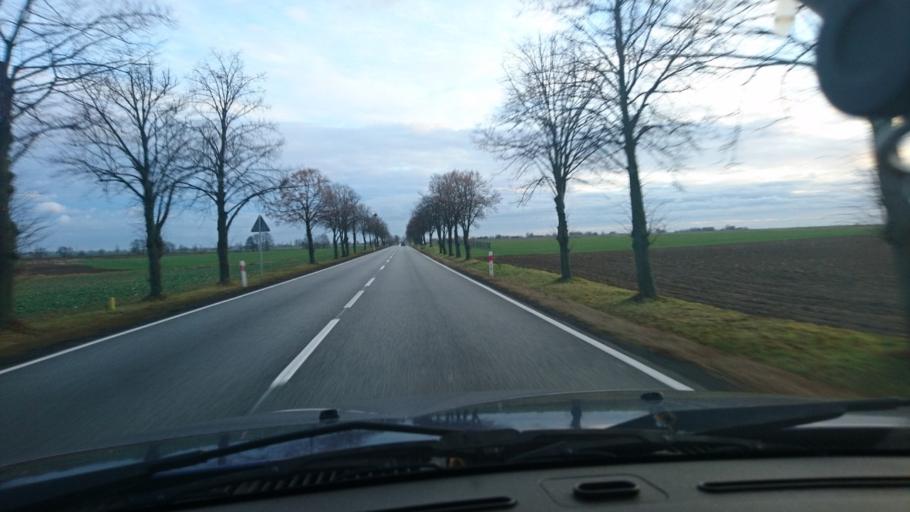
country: PL
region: Opole Voivodeship
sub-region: Powiat kluczborski
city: Kluczbork
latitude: 51.0214
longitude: 18.1953
